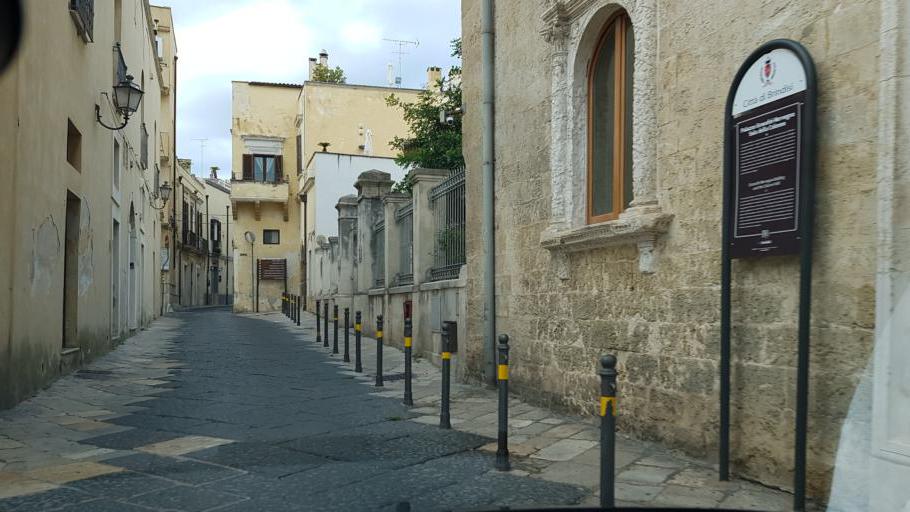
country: IT
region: Apulia
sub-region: Provincia di Brindisi
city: Brindisi
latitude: 40.6390
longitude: 17.9451
